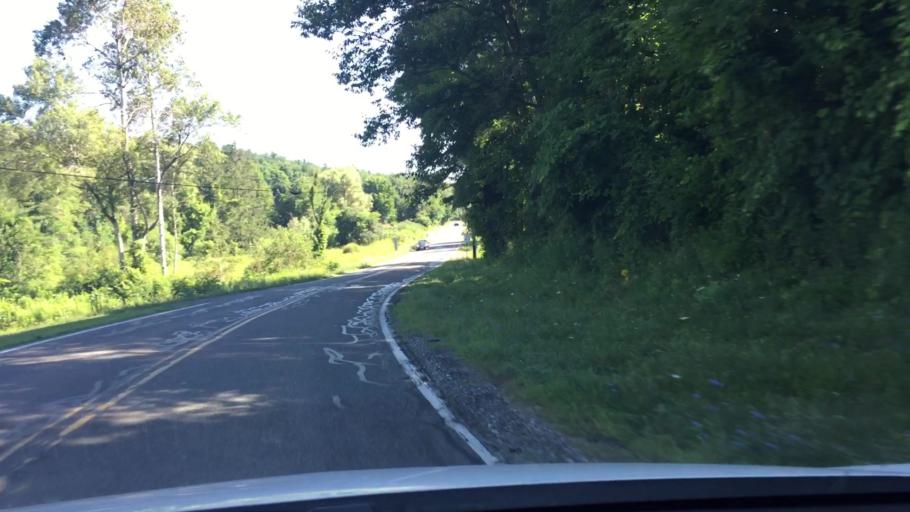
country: US
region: Massachusetts
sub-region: Berkshire County
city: West Stockbridge
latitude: 42.3473
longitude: -73.3650
